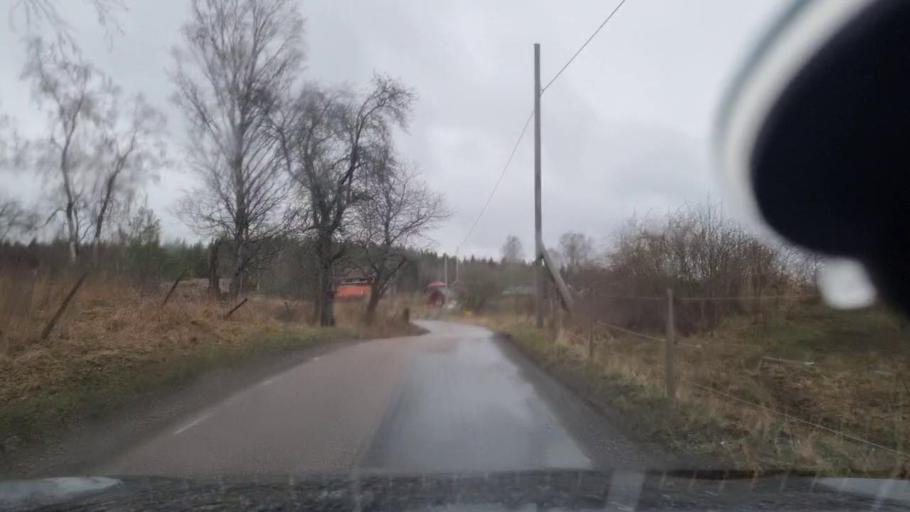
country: SE
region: Stockholm
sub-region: Taby Kommun
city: Taby
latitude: 59.4829
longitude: 18.0144
